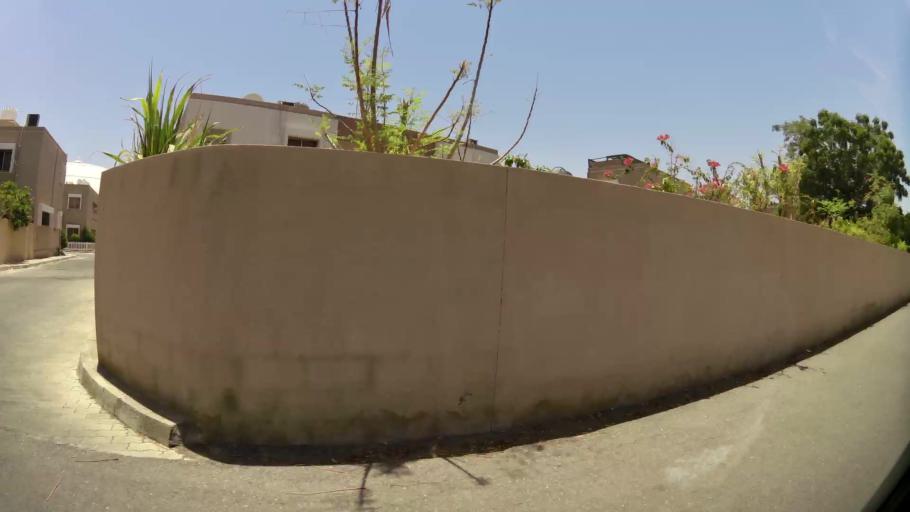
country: OM
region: Muhafazat Masqat
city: Muscat
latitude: 23.6067
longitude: 58.5375
